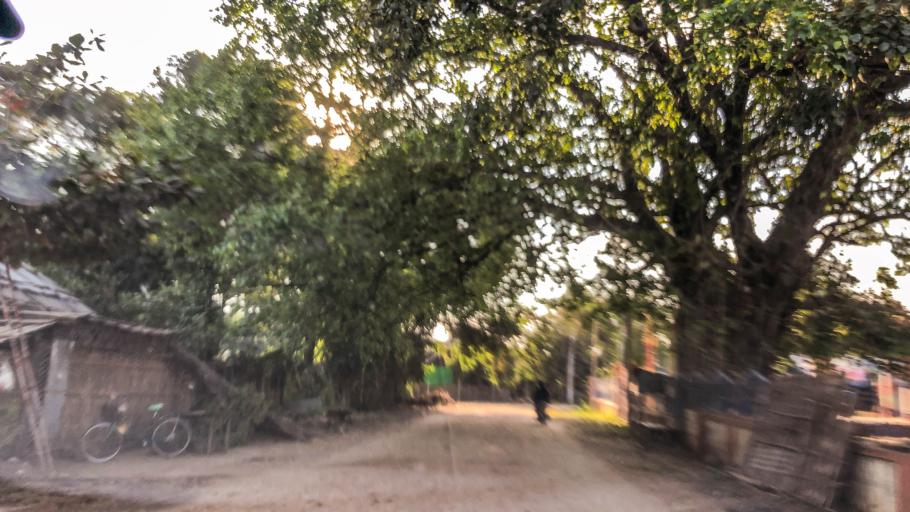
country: MM
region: Magway
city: Magway
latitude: 19.9727
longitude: 95.0401
